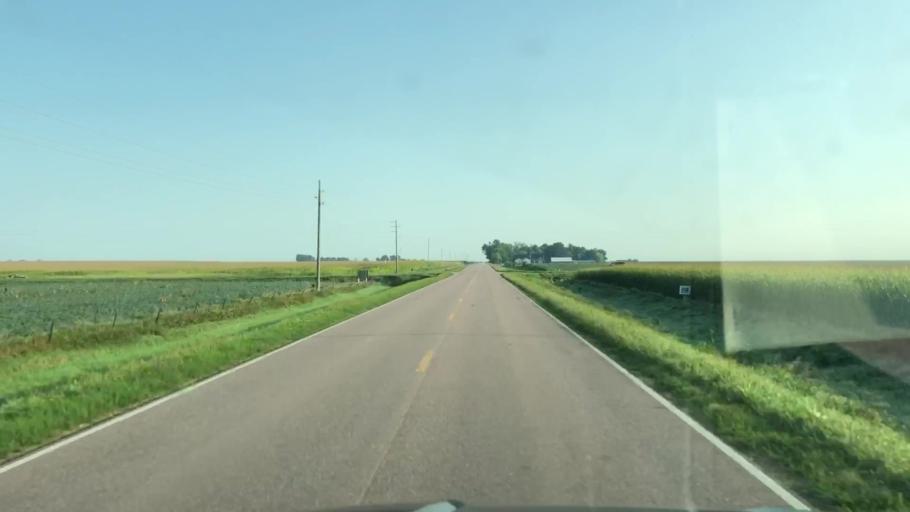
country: US
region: Iowa
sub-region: Sioux County
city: Hull
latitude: 43.1995
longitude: -96.0004
